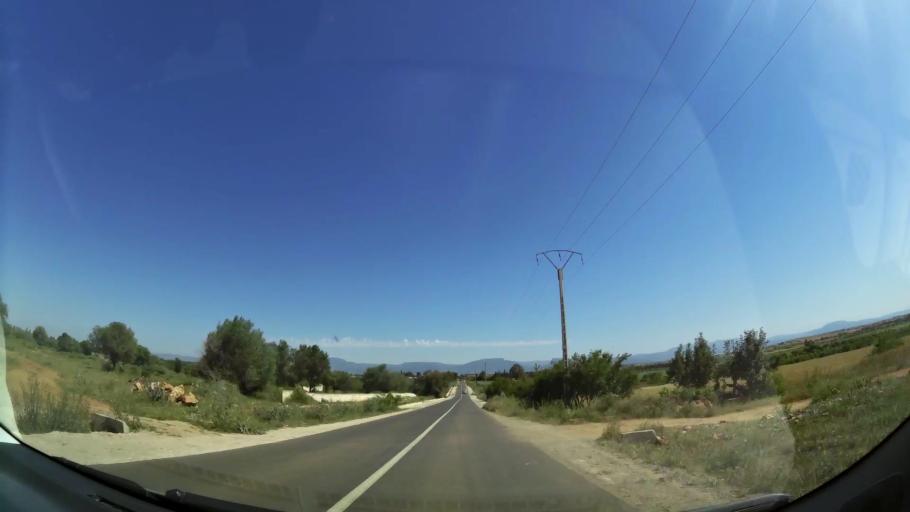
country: MA
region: Oriental
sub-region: Berkane-Taourirt
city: Madagh
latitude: 35.0242
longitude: -2.4101
